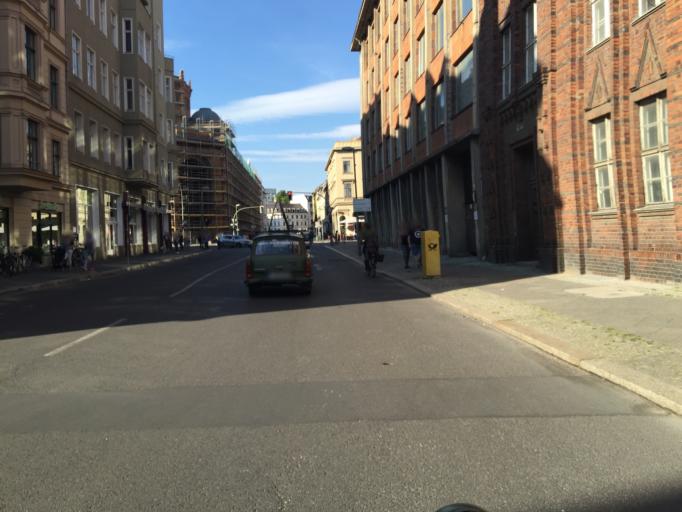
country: DE
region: Berlin
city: Mitte
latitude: 52.5244
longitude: 13.3926
